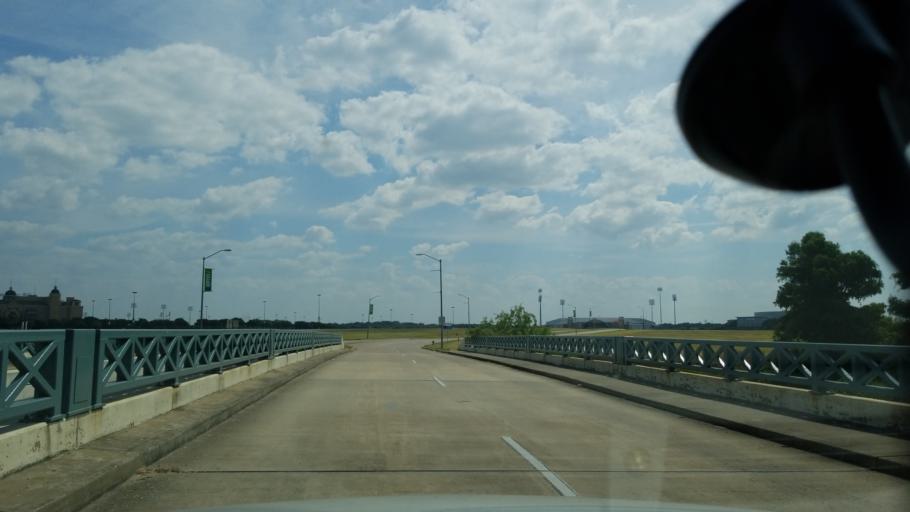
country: US
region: Texas
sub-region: Dallas County
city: Grand Prairie
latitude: 32.7672
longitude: -96.9926
